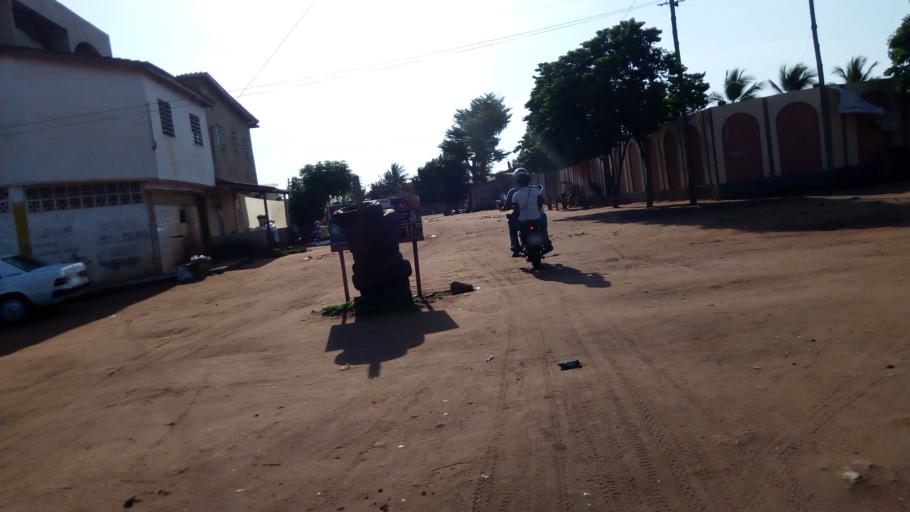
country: TG
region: Maritime
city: Lome
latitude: 6.2306
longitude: 1.1902
